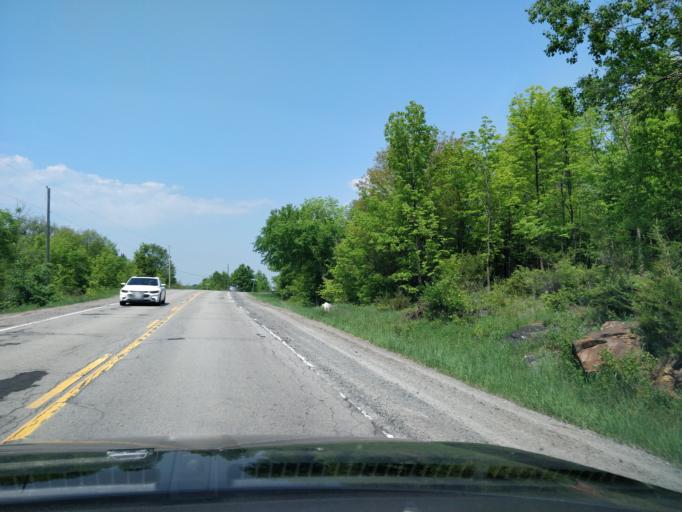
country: CA
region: Ontario
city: Perth
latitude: 44.7501
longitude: -76.3902
